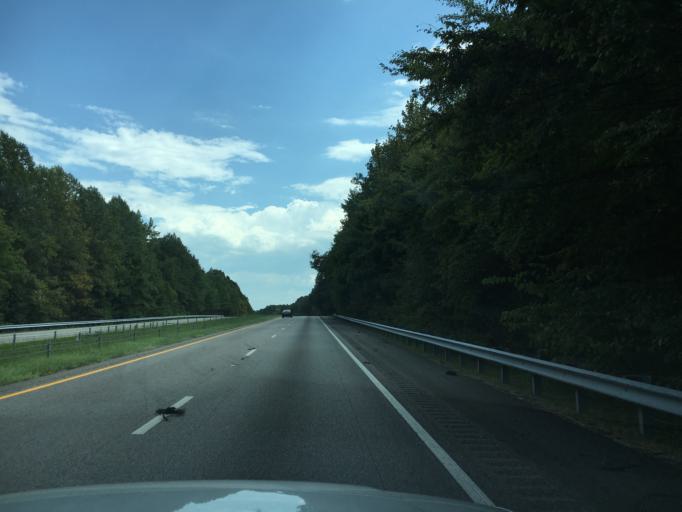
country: US
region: South Carolina
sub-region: Laurens County
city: Clinton
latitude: 34.5342
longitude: -81.8834
